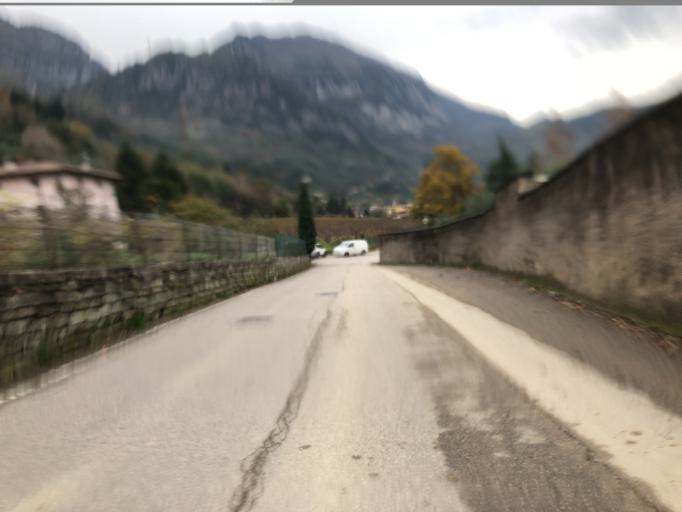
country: IT
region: Trentino-Alto Adige
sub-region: Provincia di Trento
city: Tenno
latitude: 45.9133
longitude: 10.8552
